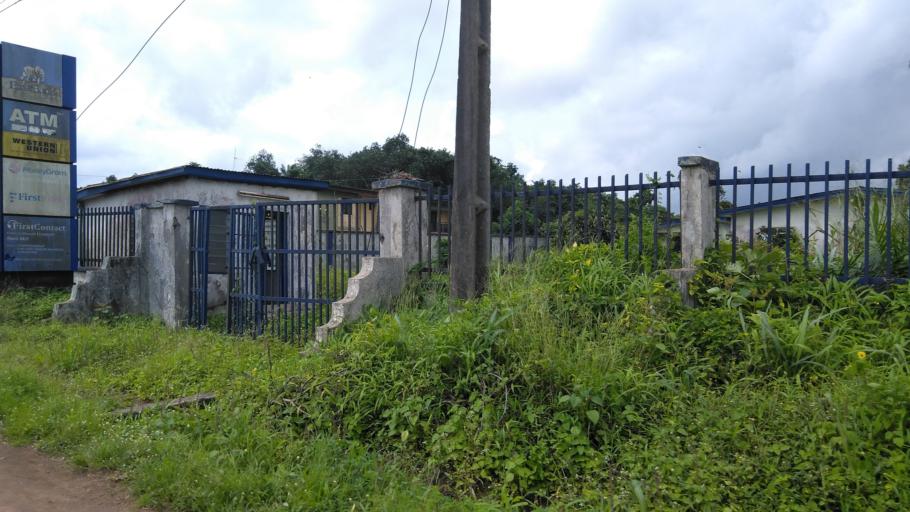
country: NG
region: Ogun
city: Abigi
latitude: 6.6039
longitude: 4.4886
